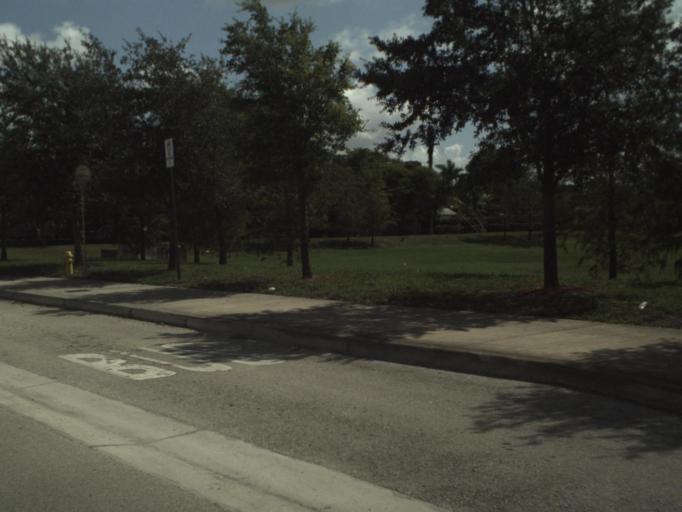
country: US
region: Florida
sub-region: Broward County
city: Miami Gardens
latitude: 25.9779
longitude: -80.2062
